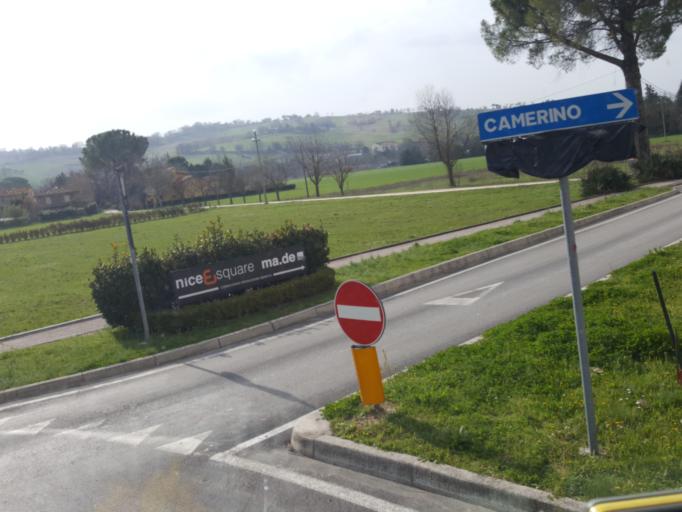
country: IT
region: The Marches
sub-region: Provincia di Macerata
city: Passo di Treia
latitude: 43.2800
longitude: 13.3231
